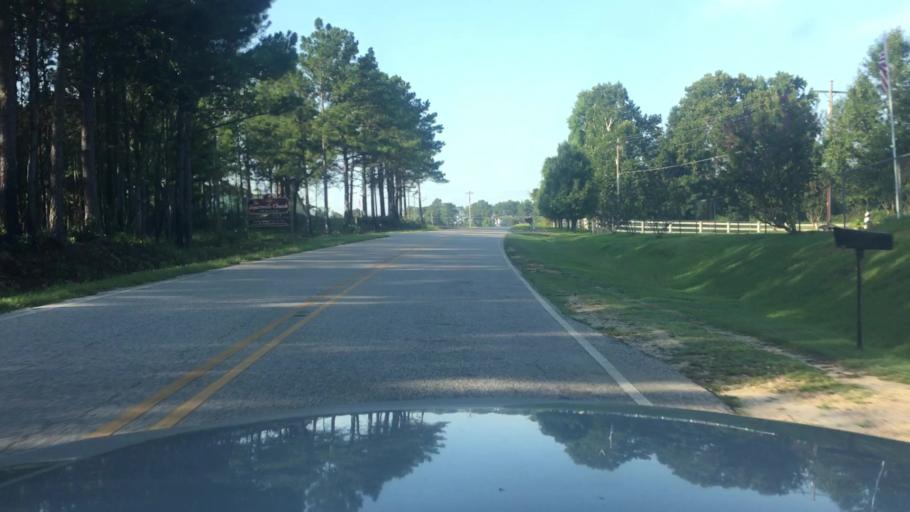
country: US
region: North Carolina
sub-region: Cumberland County
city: Spring Lake
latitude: 35.2160
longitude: -78.8942
